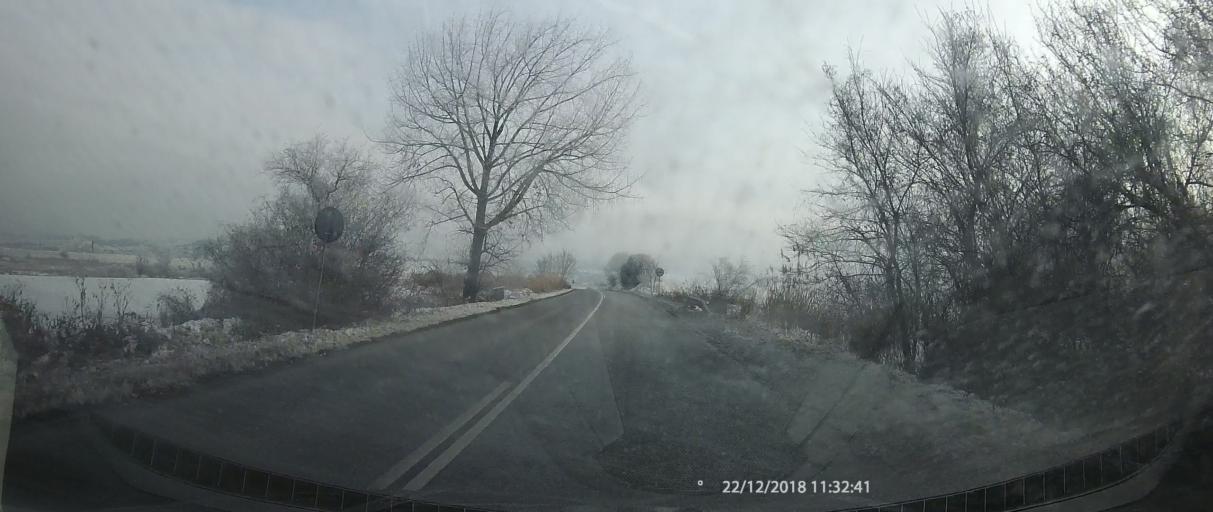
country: BG
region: Kyustendil
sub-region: Obshtina Dupnitsa
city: Dupnitsa
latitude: 42.2724
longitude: 23.0294
